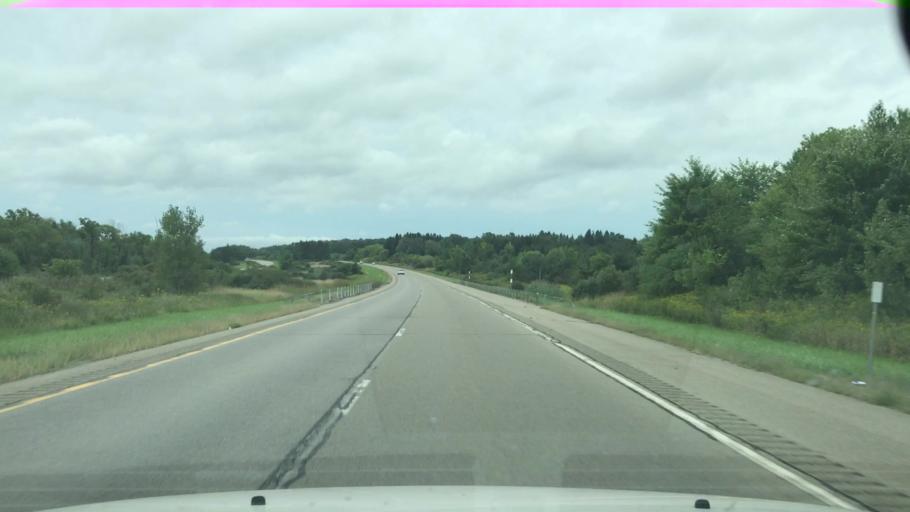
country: US
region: New York
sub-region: Erie County
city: North Boston
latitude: 42.6203
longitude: -78.7640
